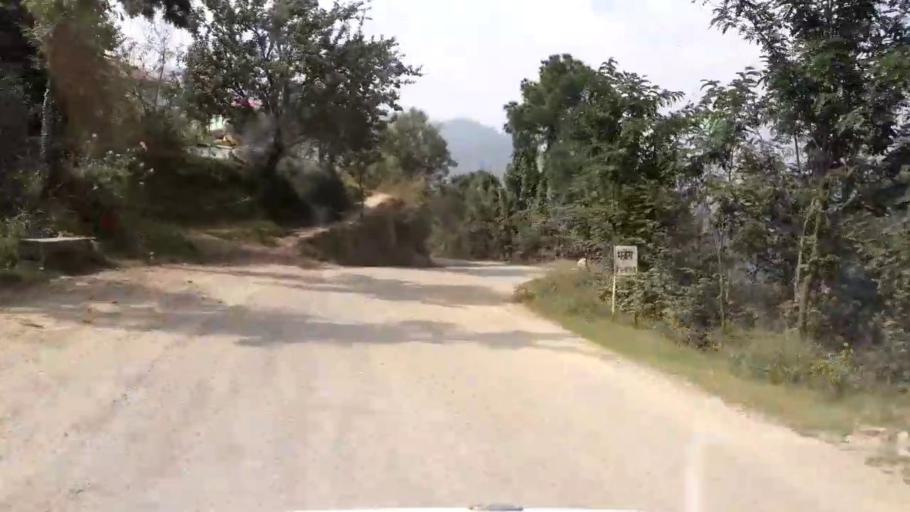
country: IN
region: Himachal Pradesh
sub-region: Shimla
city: Shimla
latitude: 31.0590
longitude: 77.1556
